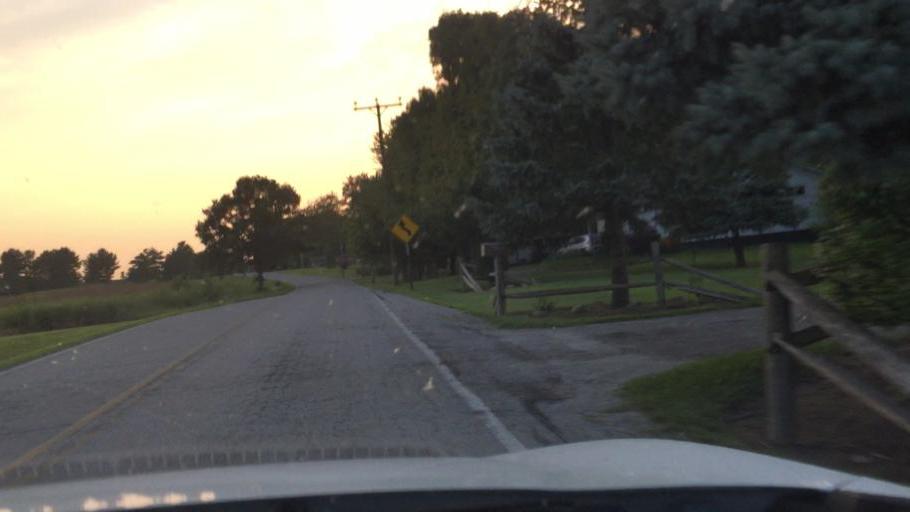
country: US
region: Ohio
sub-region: Madison County
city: Choctaw Lake
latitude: 39.9469
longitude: -83.5260
